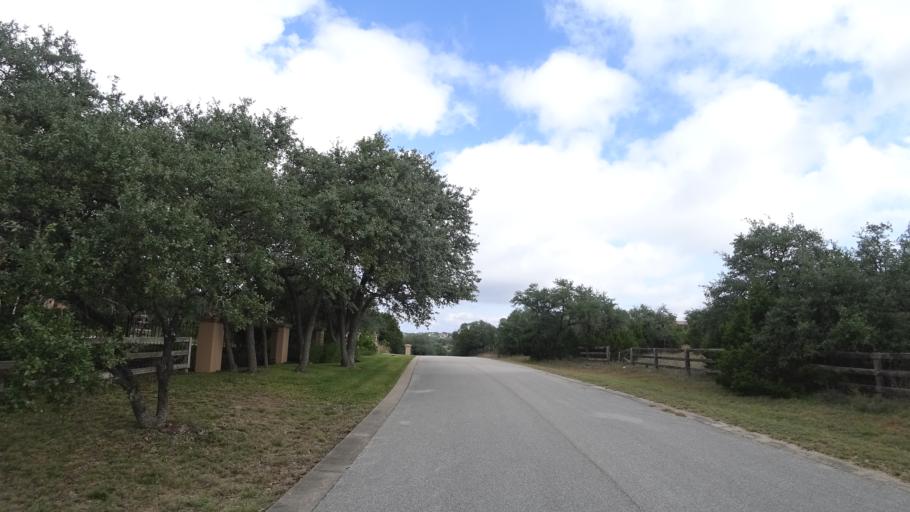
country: US
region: Texas
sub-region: Travis County
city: Barton Creek
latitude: 30.3042
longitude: -97.8971
